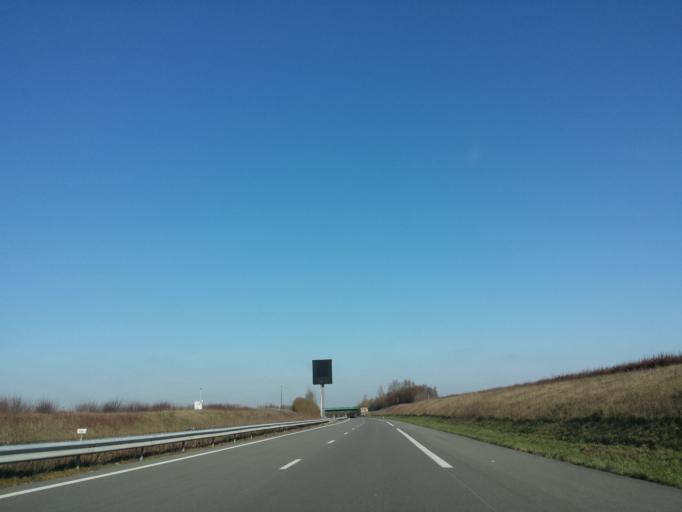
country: FR
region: Picardie
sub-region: Departement de l'Oise
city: Breteuil
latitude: 49.7050
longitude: 2.2374
